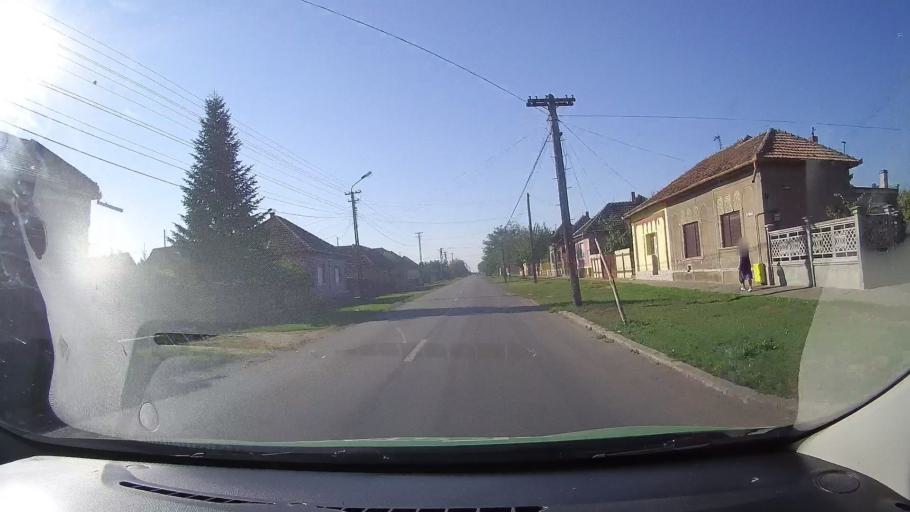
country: RO
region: Satu Mare
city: Carei
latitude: 47.6761
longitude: 22.4694
